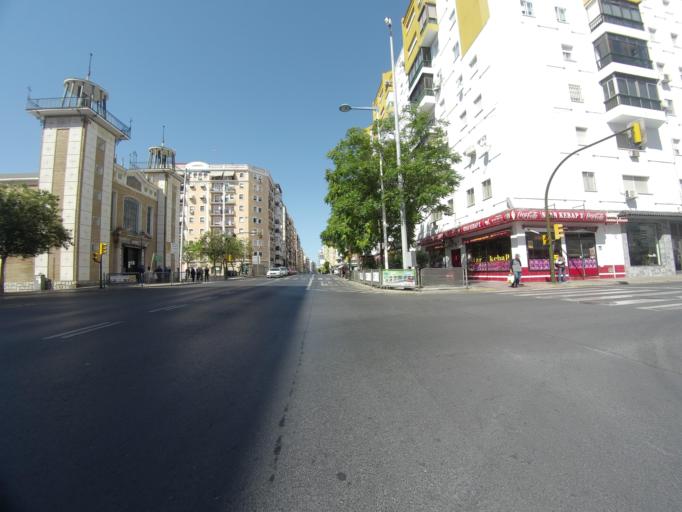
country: ES
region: Andalusia
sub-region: Provincia de Huelva
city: Huelva
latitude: 37.2603
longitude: -6.9313
